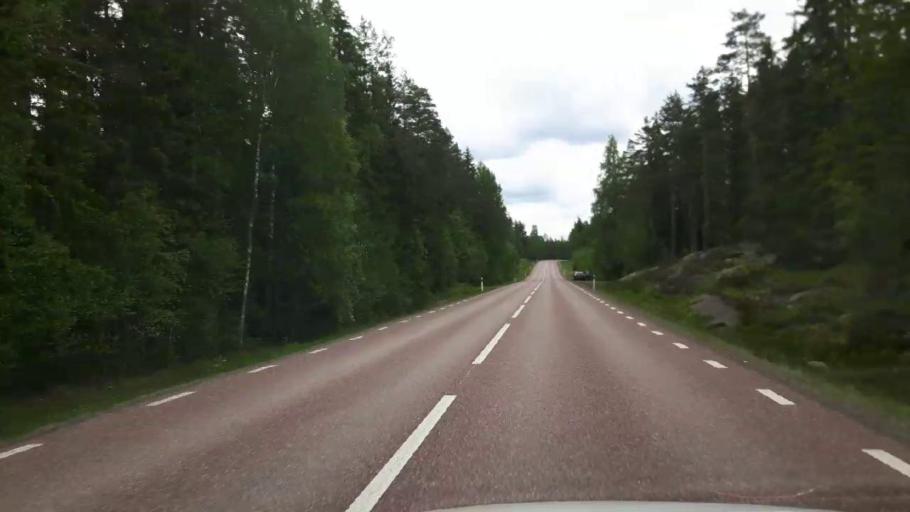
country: SE
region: Dalarna
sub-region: Hedemora Kommun
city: Brunna
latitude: 60.1936
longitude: 15.9982
